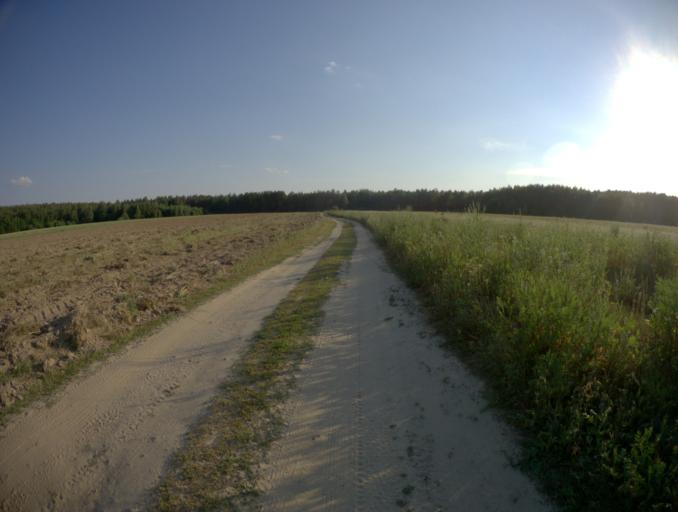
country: RU
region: Vladimir
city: Kommunar
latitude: 56.0432
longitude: 40.4716
